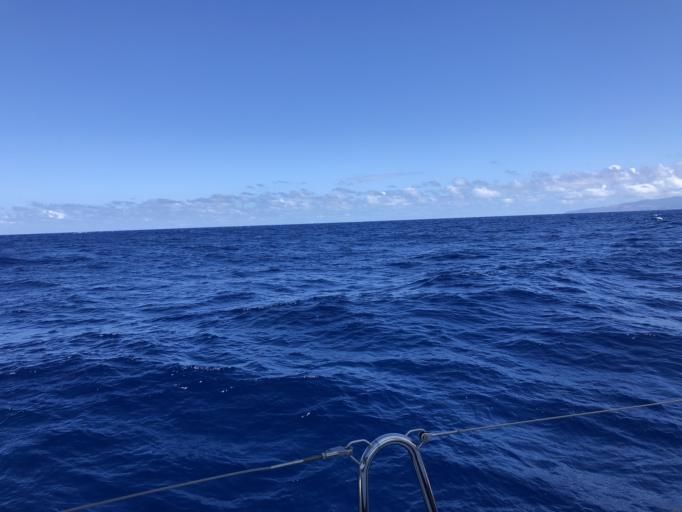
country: PT
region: Azores
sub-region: Vila Franca do Campo
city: Vila Franca do Campo
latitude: 37.1255
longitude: -25.3473
